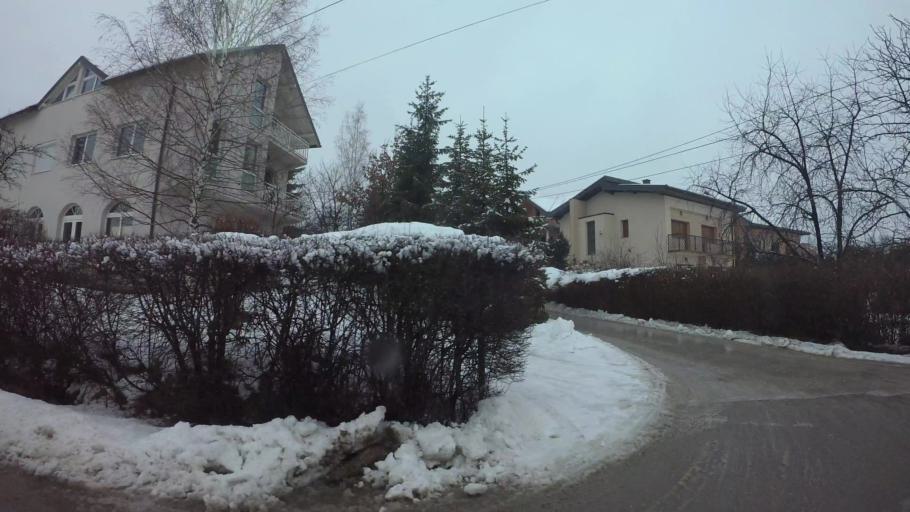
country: BA
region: Federation of Bosnia and Herzegovina
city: Hadzici
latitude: 43.8468
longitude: 18.2774
